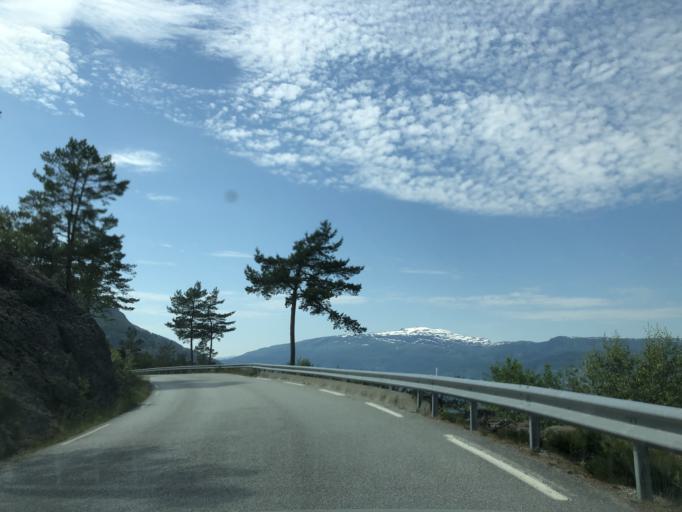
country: NO
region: Hordaland
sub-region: Jondal
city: Jondal
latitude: 60.3137
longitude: 6.3100
